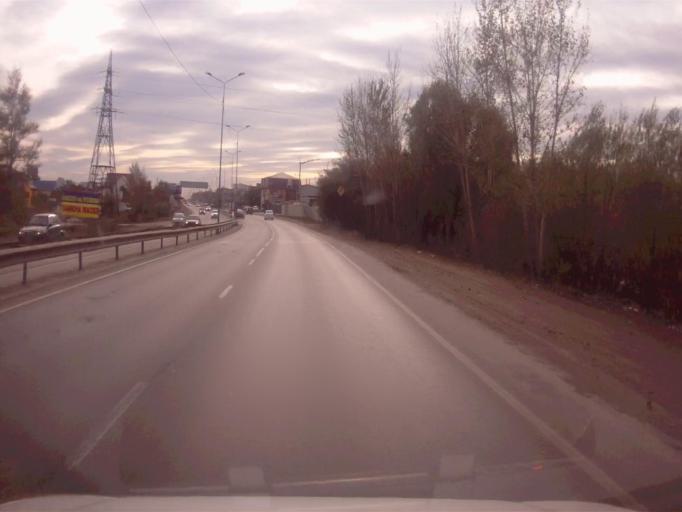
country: RU
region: Chelyabinsk
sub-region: Gorod Chelyabinsk
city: Chelyabinsk
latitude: 55.1127
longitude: 61.4115
